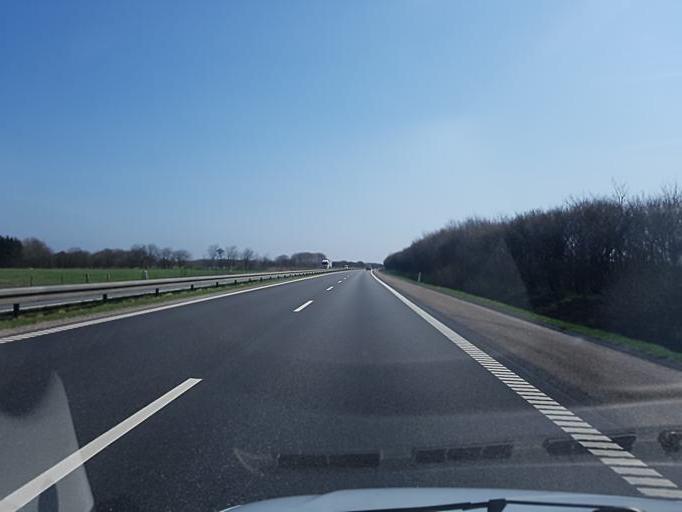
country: DK
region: South Denmark
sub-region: Esbjerg Kommune
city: Bramming
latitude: 55.5138
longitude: 8.7638
